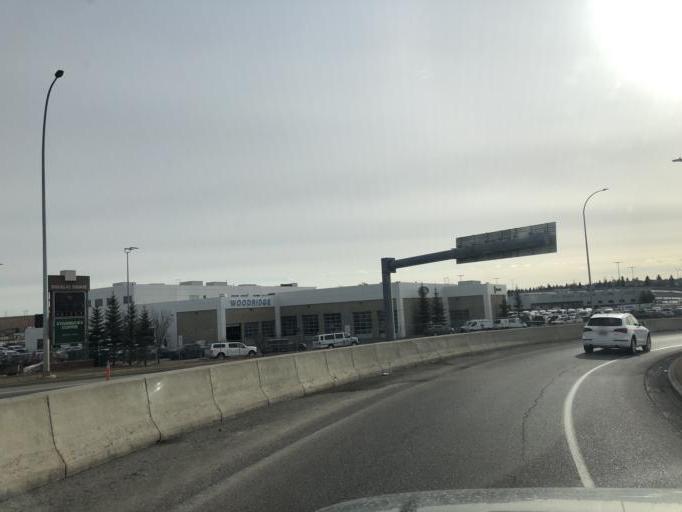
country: CA
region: Alberta
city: Calgary
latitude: 50.9497
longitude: -114.0027
